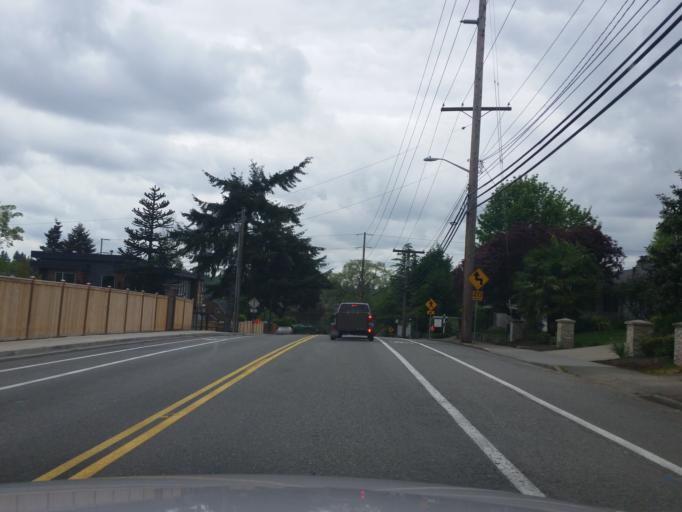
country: US
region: Washington
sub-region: King County
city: Kirkland
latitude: 47.6741
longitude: -122.1963
